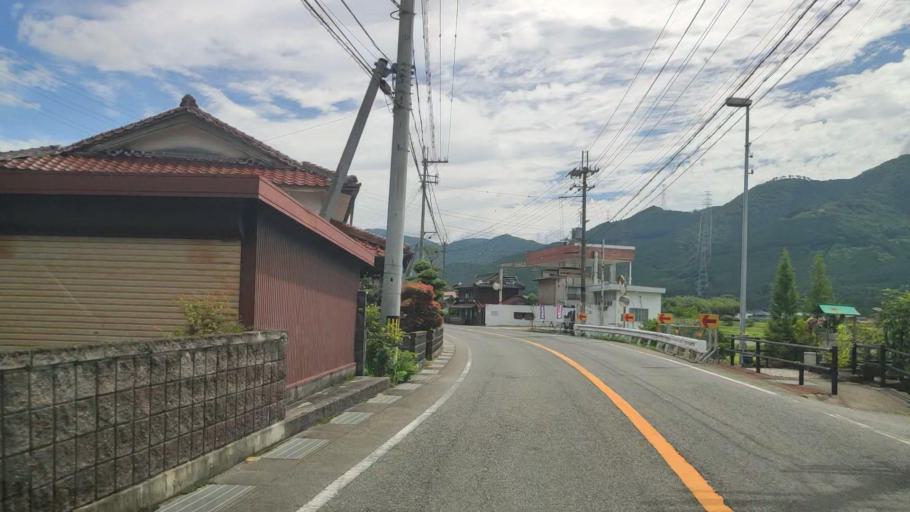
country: JP
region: Hyogo
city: Nishiwaki
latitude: 35.1099
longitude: 134.9090
